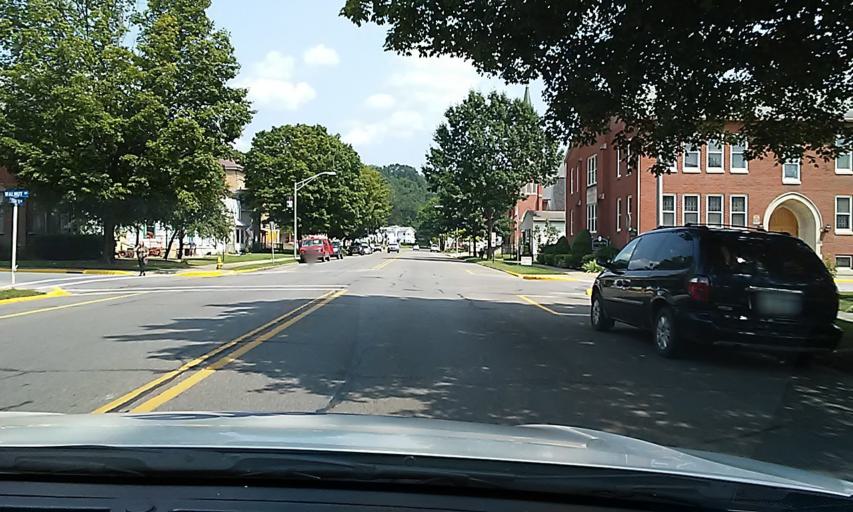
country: US
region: Pennsylvania
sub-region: Cameron County
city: Emporium
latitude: 41.5117
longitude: -78.2339
